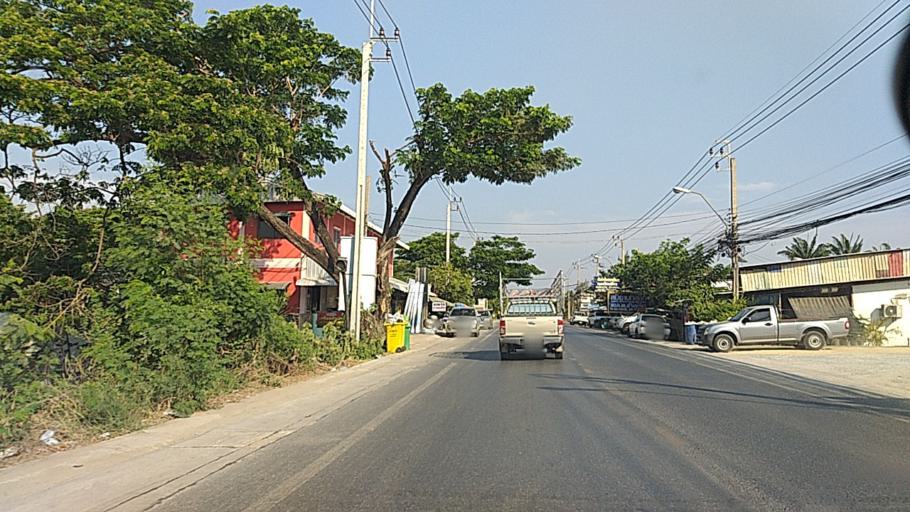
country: TH
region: Nonthaburi
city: Bang Bua Thong
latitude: 13.9329
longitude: 100.3737
